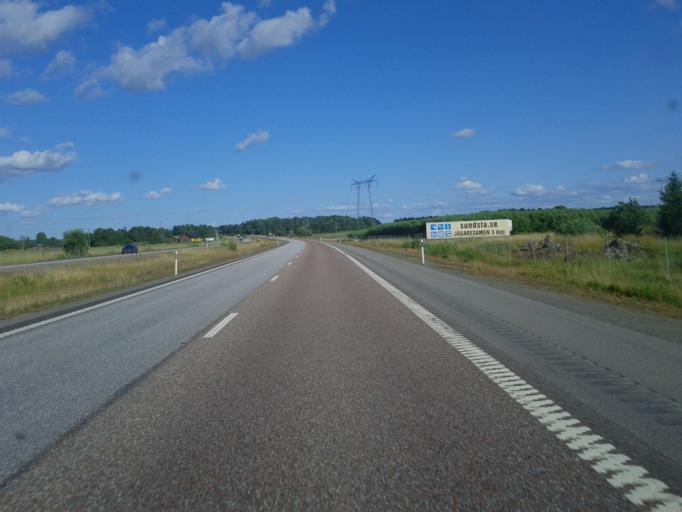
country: SE
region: Uppsala
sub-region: Habo Kommun
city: Balsta
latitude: 59.5970
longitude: 17.4502
